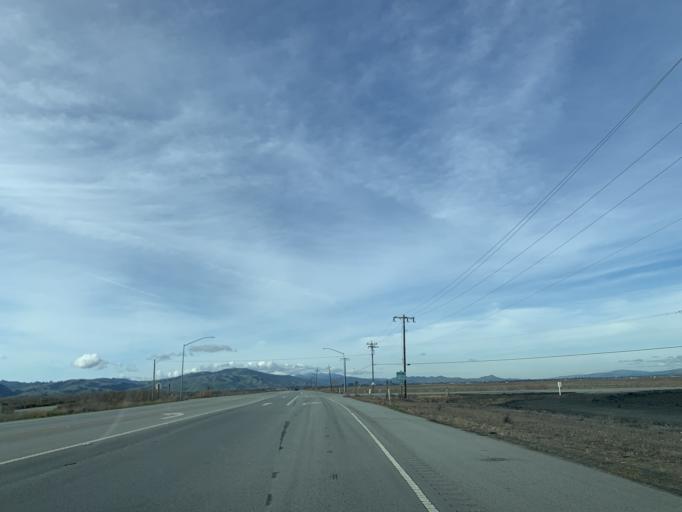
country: US
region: California
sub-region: San Benito County
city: San Juan Bautista
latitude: 36.9306
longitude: -121.4752
